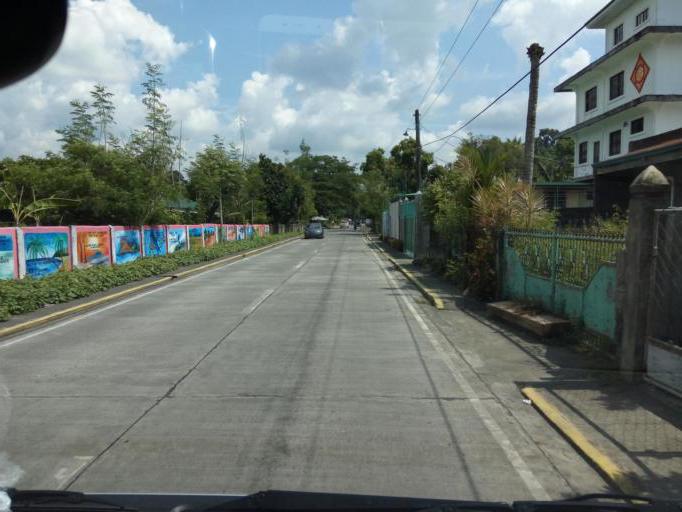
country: PH
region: Central Luzon
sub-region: Province of Aurora
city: Maria Aurora
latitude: 15.7969
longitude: 121.4758
